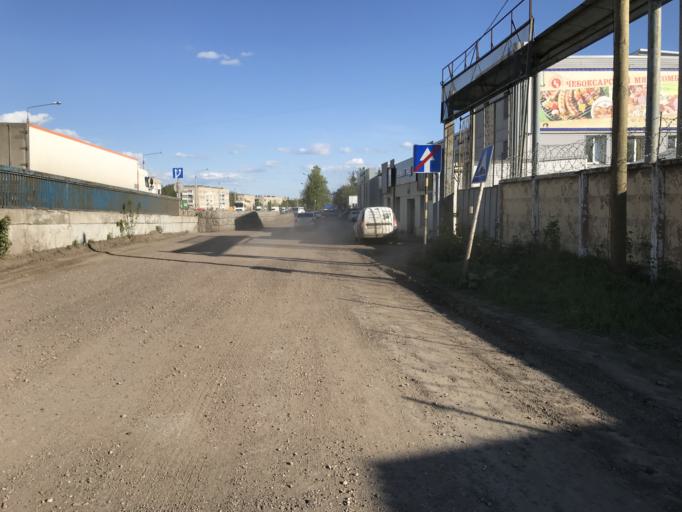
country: RU
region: Chuvashia
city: Kanash
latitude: 55.5030
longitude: 47.4673
